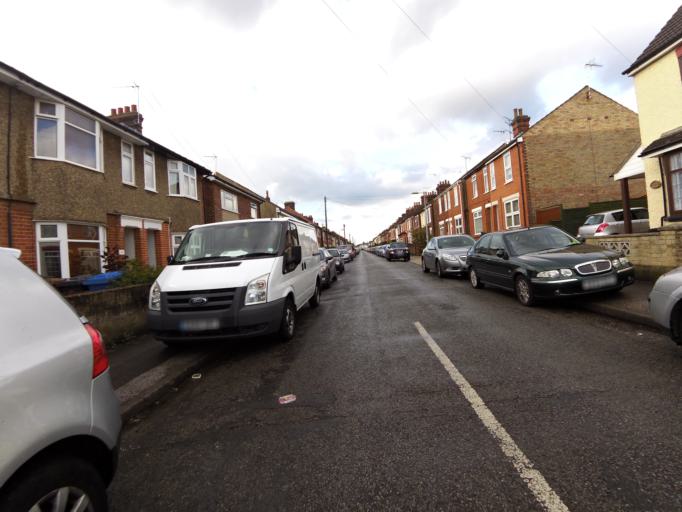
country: GB
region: England
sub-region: Suffolk
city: Ipswich
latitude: 52.0488
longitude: 1.1876
